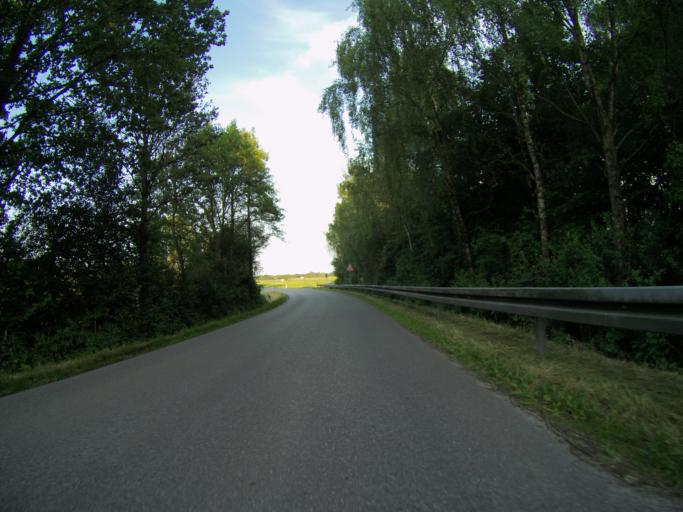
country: DE
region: Bavaria
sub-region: Upper Bavaria
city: Marzling
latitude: 48.3888
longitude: 11.7928
